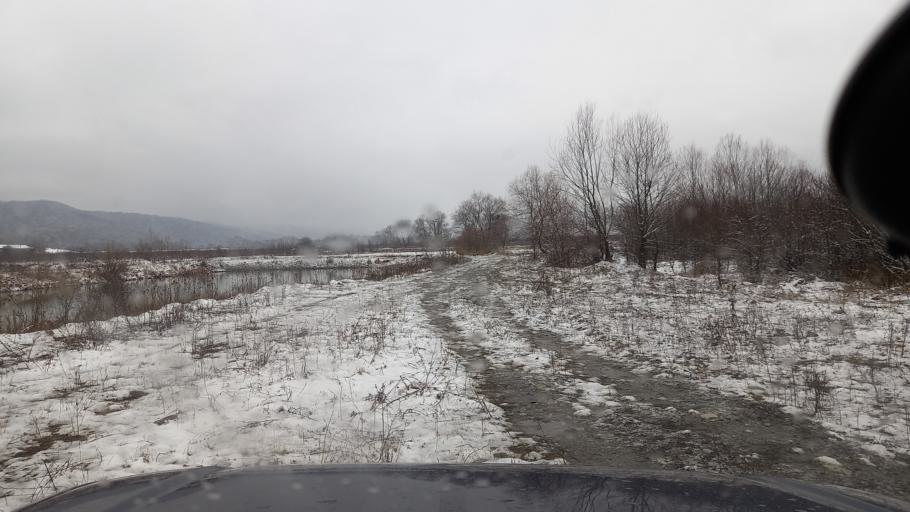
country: RU
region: Adygeya
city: Kamennomostskiy
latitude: 44.2285
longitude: 40.1825
